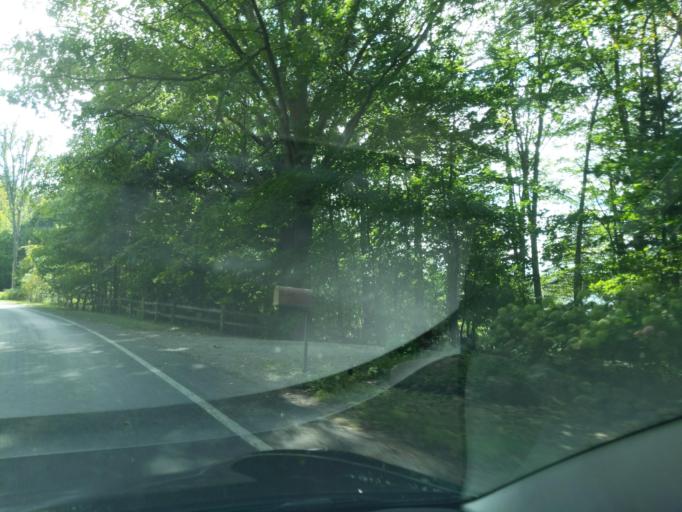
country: US
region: Michigan
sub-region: Antrim County
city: Bellaire
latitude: 45.0059
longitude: -85.2938
